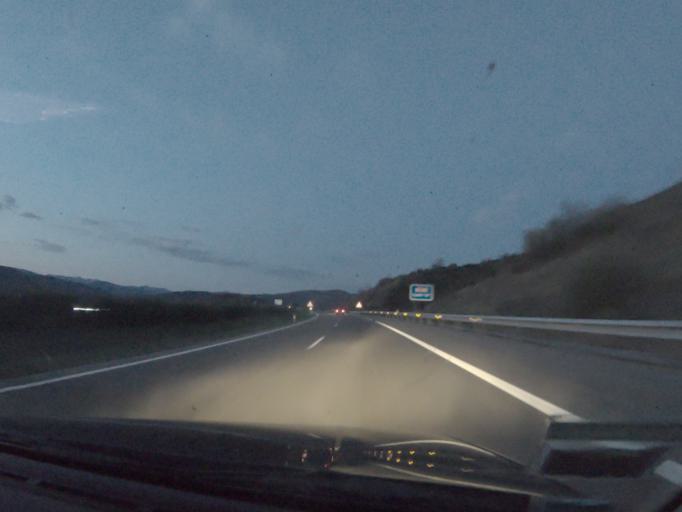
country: ES
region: Castille and Leon
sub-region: Provincia de Leon
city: Folgoso de la Ribera
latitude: 42.6185
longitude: -6.3252
